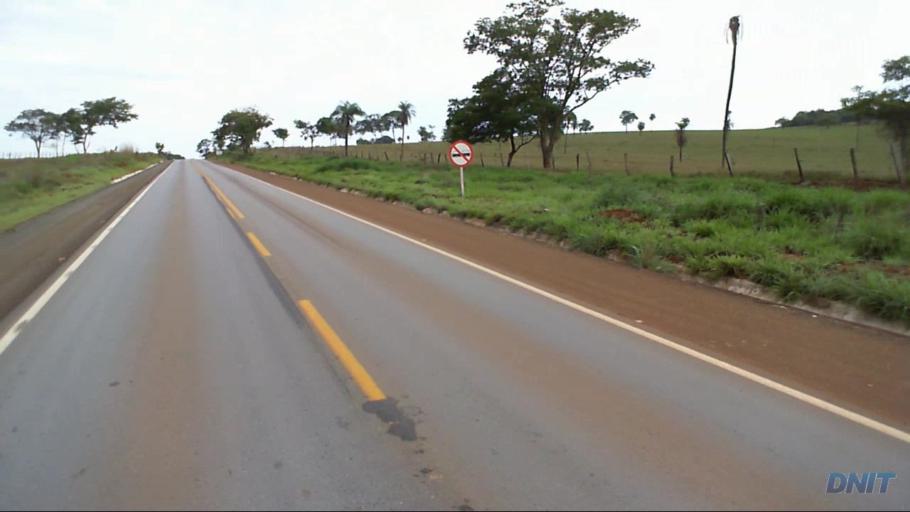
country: BR
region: Goias
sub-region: Uruacu
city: Uruacu
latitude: -14.6872
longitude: -49.1303
